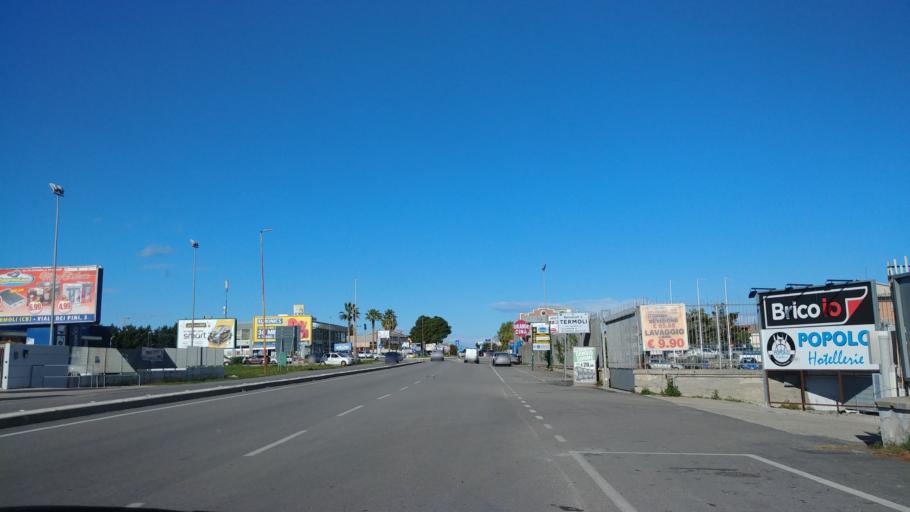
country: IT
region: Molise
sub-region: Provincia di Campobasso
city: Termoli
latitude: 41.9812
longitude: 15.0070
